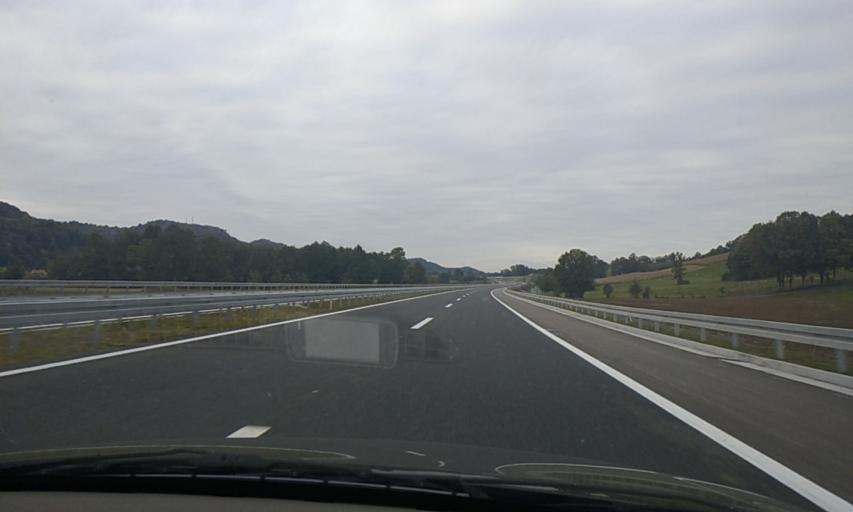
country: BA
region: Republika Srpska
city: Maglajani
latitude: 44.8690
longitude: 17.4249
